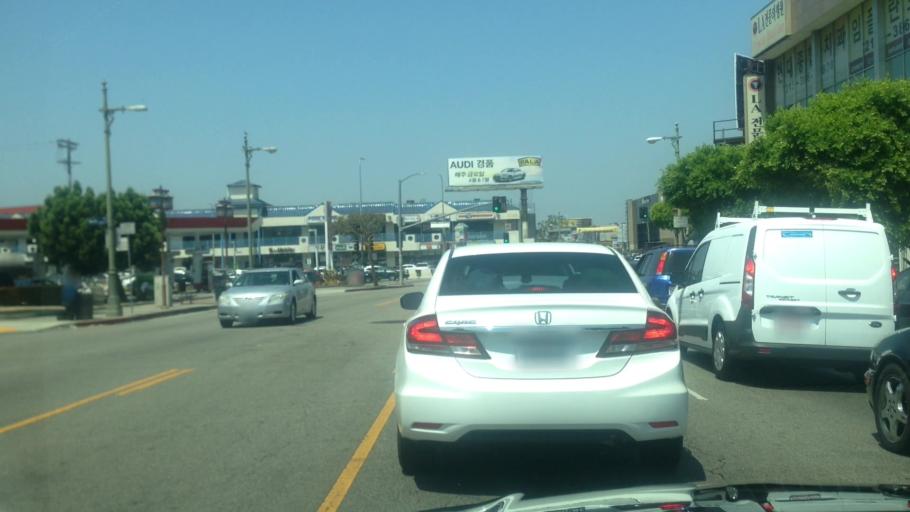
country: US
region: California
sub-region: Los Angeles County
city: Echo Park
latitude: 34.0524
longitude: -118.2904
